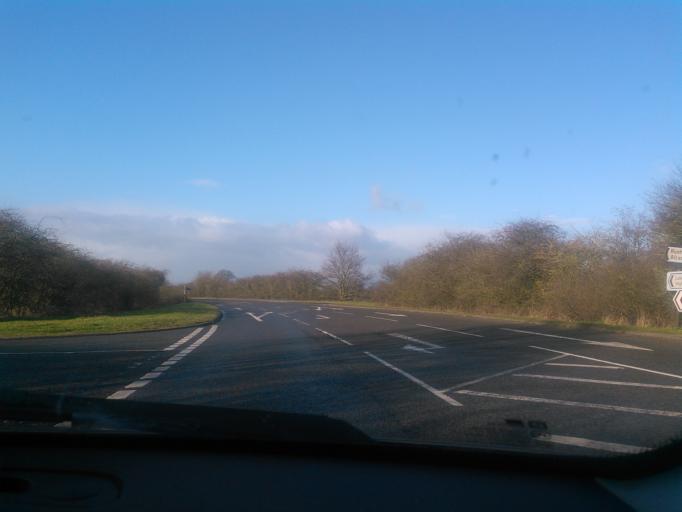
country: GB
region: England
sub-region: Telford and Wrekin
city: Eyton upon the Weald Moors
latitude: 52.7308
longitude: -2.5488
